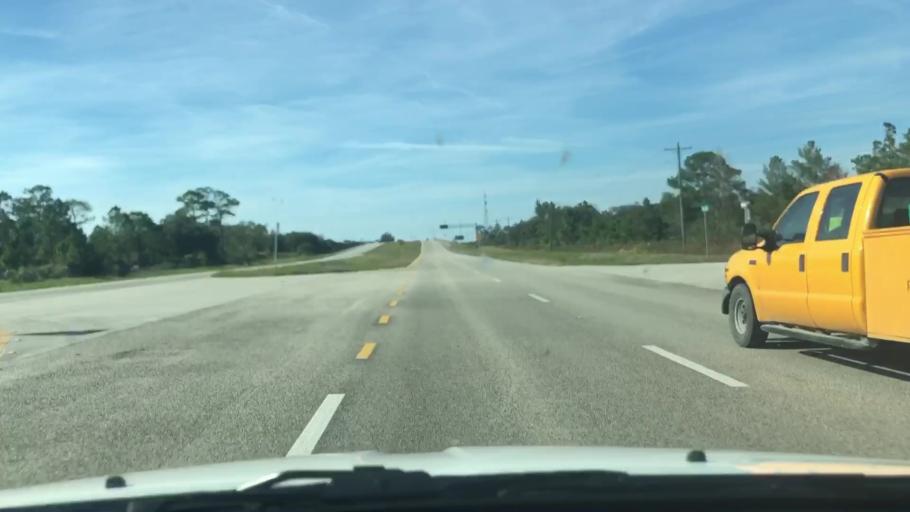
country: US
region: Florida
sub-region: Indian River County
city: Fellsmere
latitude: 27.6931
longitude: -80.8888
